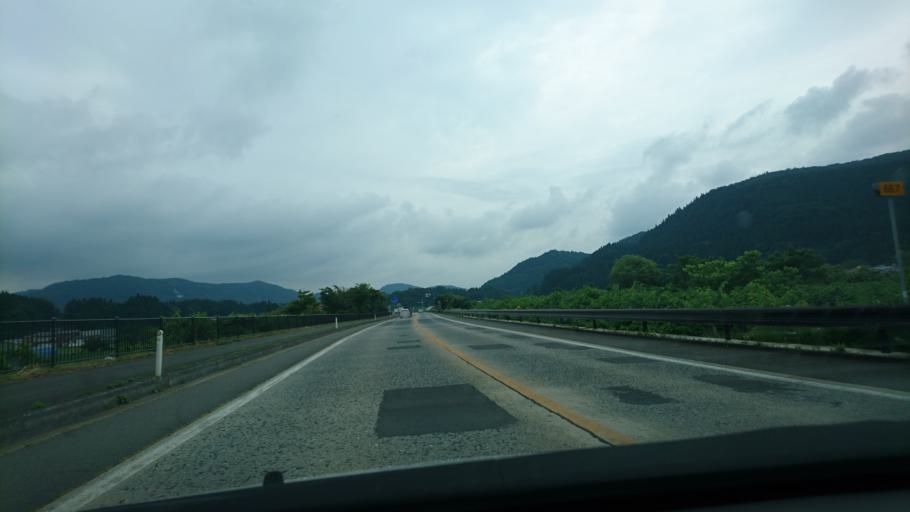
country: JP
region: Miyagi
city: Furukawa
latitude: 38.7358
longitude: 140.7655
